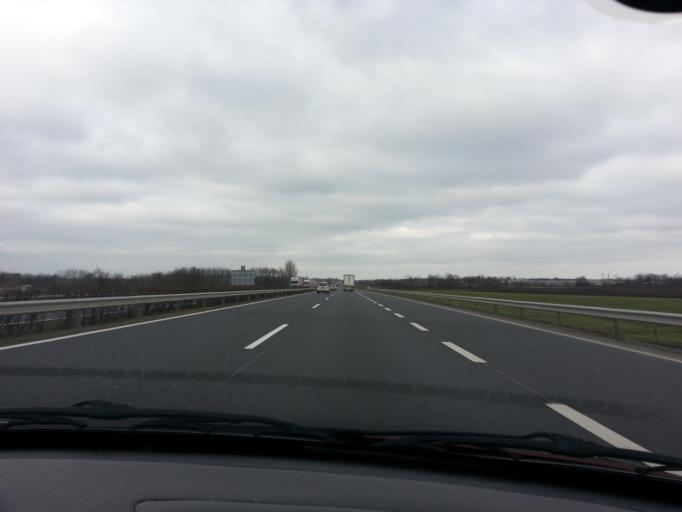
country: HU
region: Bacs-Kiskun
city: Kiskunfelegyhaza
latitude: 46.6809
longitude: 19.8207
